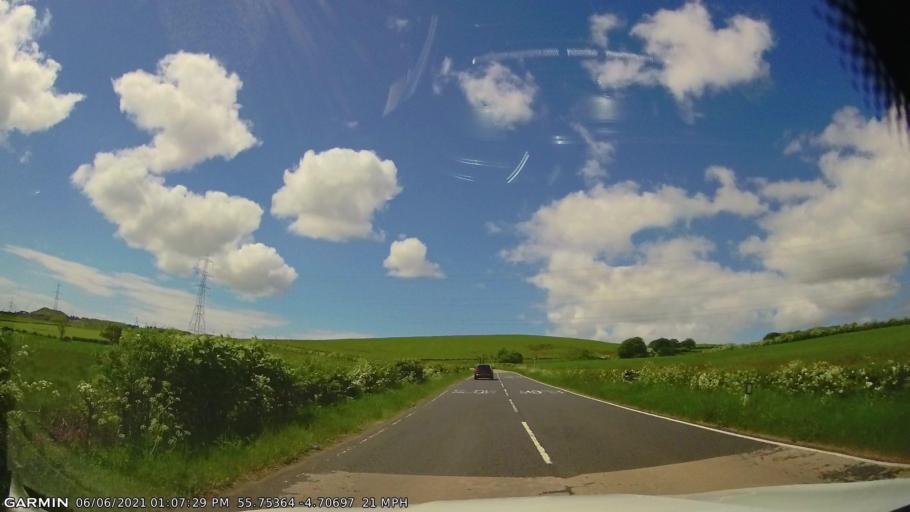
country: GB
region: Scotland
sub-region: North Ayrshire
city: Kilbirnie
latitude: 55.7535
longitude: -4.7069
